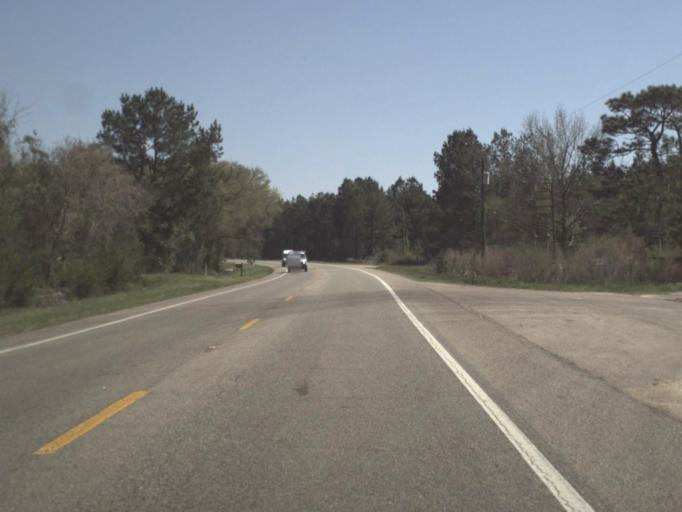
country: US
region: Florida
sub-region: Calhoun County
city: Blountstown
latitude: 30.4281
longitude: -85.1674
